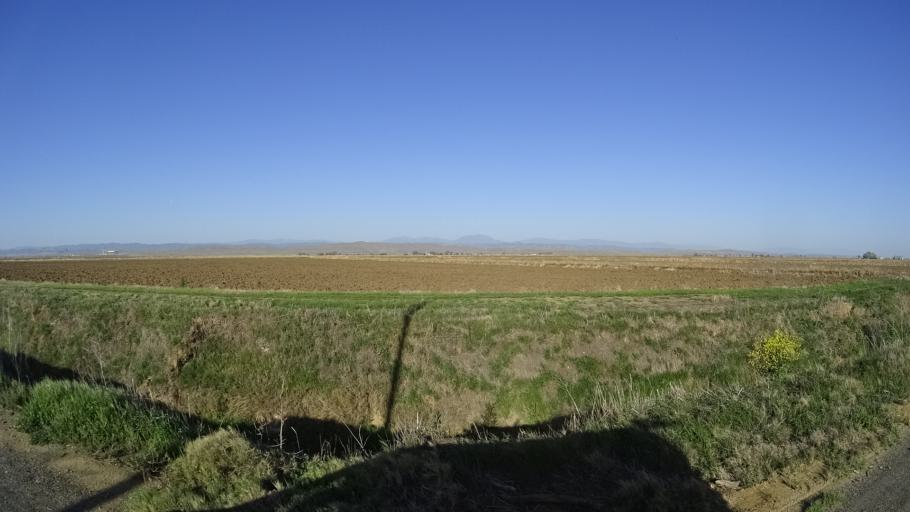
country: US
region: California
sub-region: Colusa County
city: Maxwell
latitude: 39.3956
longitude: -122.2301
